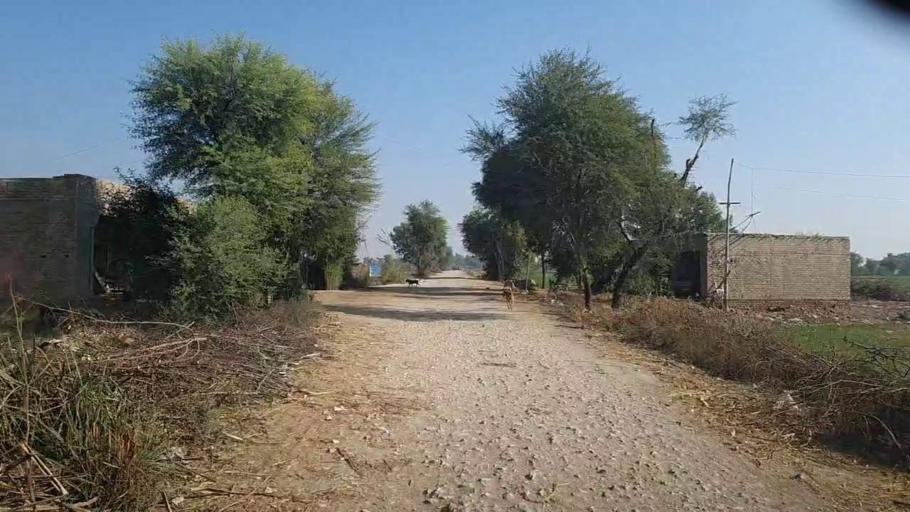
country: PK
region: Sindh
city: Darya Khan Marri
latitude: 26.6558
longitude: 68.3530
